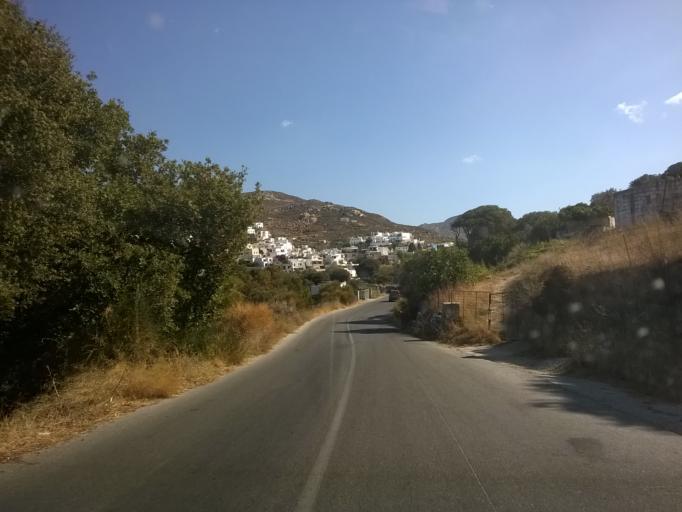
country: GR
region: South Aegean
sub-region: Nomos Kykladon
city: Filotion
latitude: 37.0990
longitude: 25.4753
